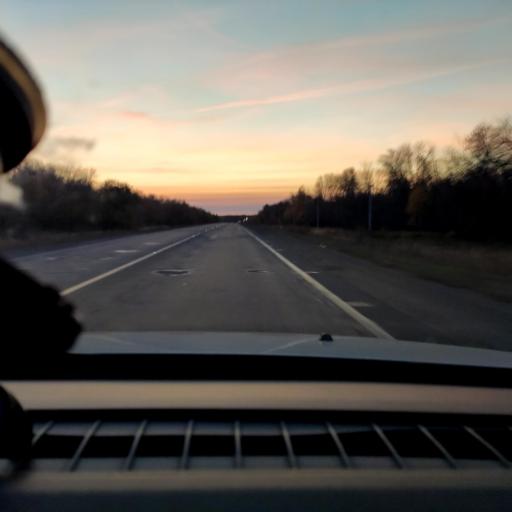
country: RU
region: Samara
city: Novokuybyshevsk
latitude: 52.9868
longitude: 49.8625
